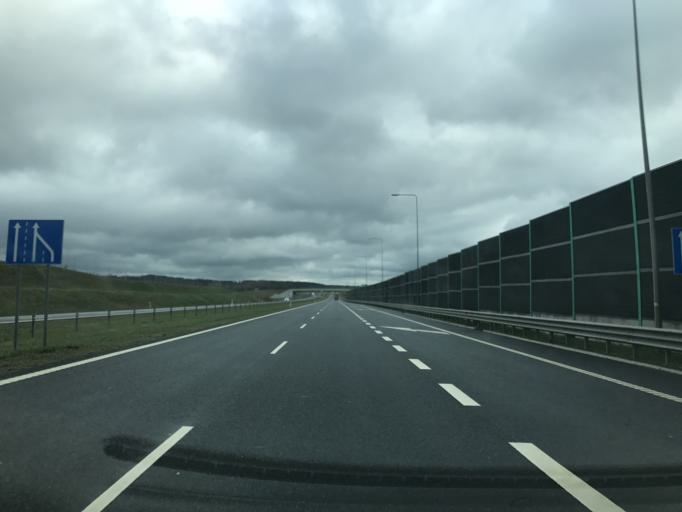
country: PL
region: Warmian-Masurian Voivodeship
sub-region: Powiat olsztynski
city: Olsztynek
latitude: 53.5711
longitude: 20.2608
